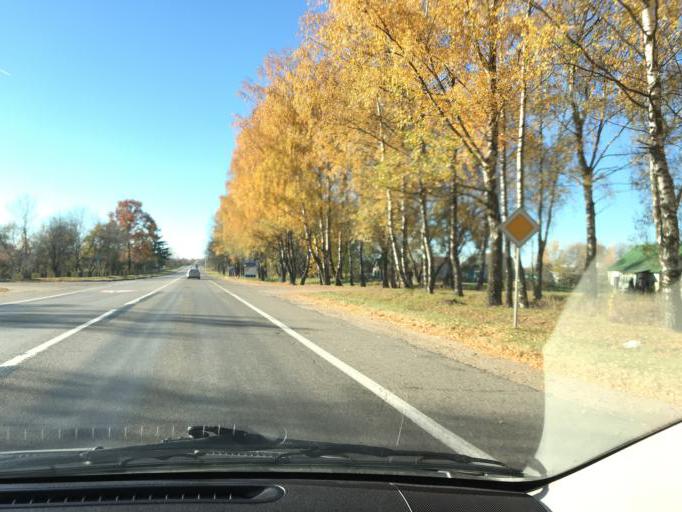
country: BY
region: Vitebsk
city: Lyepyel'
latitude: 54.9431
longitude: 28.7738
